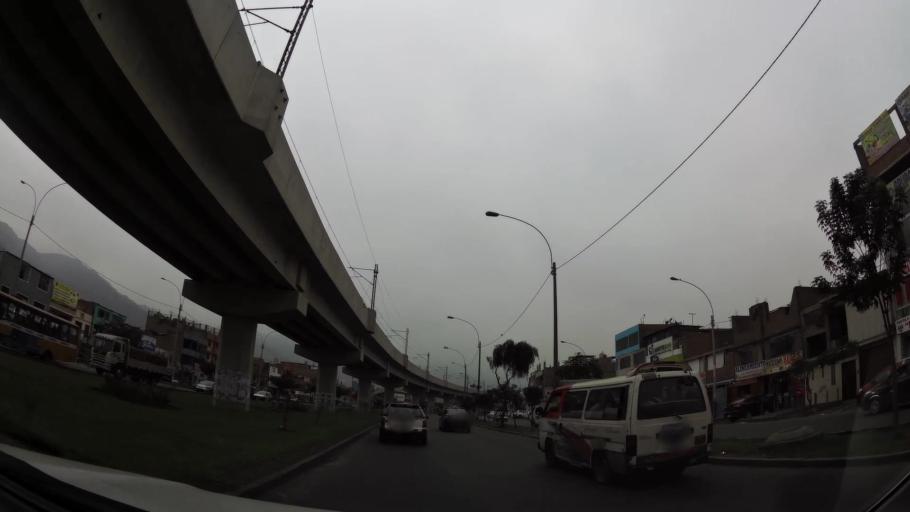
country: PE
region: Lima
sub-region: Lima
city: Independencia
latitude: -11.9931
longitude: -77.0108
